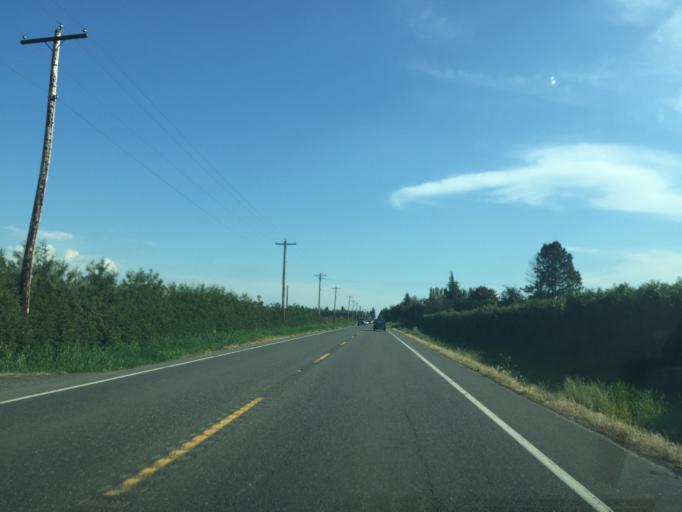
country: US
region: Washington
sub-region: Whatcom County
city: Lynden
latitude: 48.9564
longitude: -122.4853
